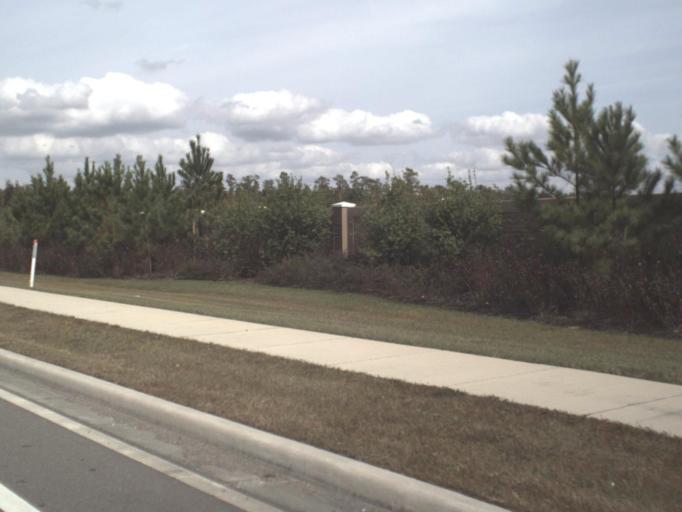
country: US
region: Florida
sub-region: Osceola County
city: Campbell
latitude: 28.2365
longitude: -81.4872
